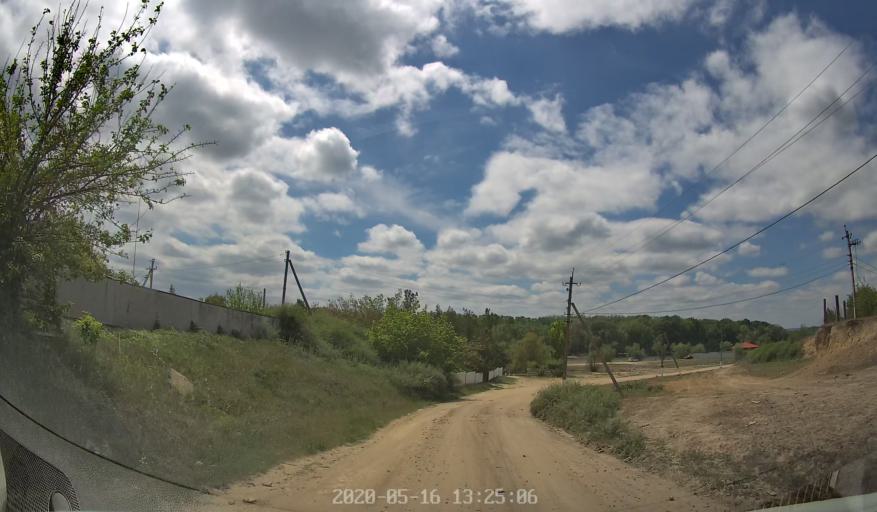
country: MD
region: Telenesti
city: Dnestrovsc
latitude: 46.5466
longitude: 30.0085
